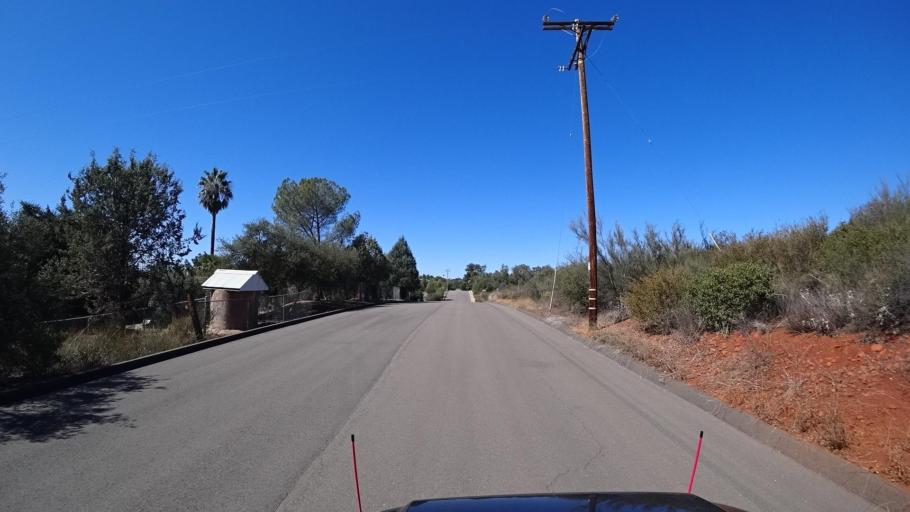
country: US
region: California
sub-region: San Diego County
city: Alpine
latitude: 32.8377
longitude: -116.7379
